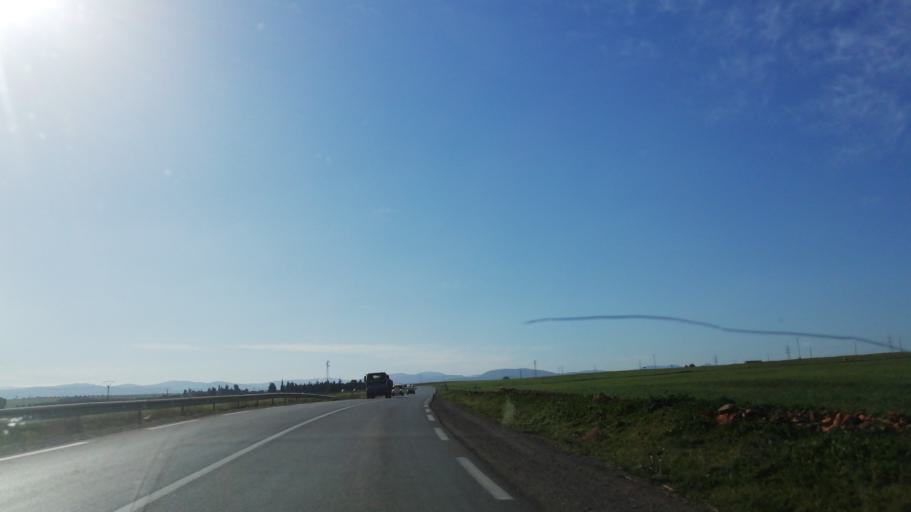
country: DZ
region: Tlemcen
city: Ouled Mimoun
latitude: 34.9985
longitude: -0.9077
